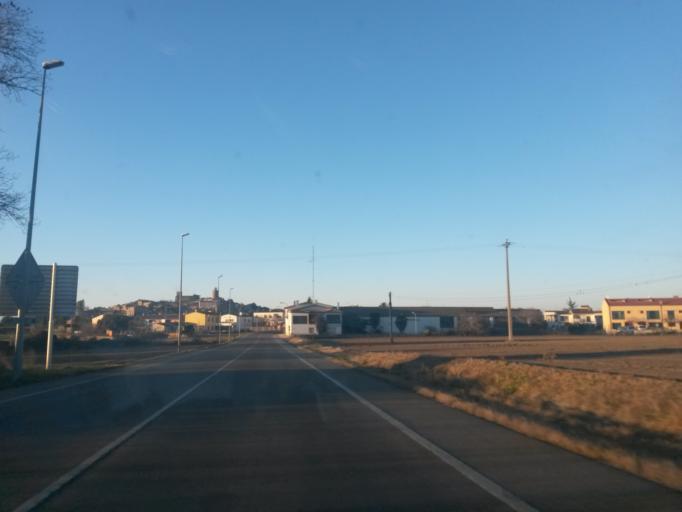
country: ES
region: Catalonia
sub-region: Provincia de Girona
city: Pals
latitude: 41.9663
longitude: 3.1494
